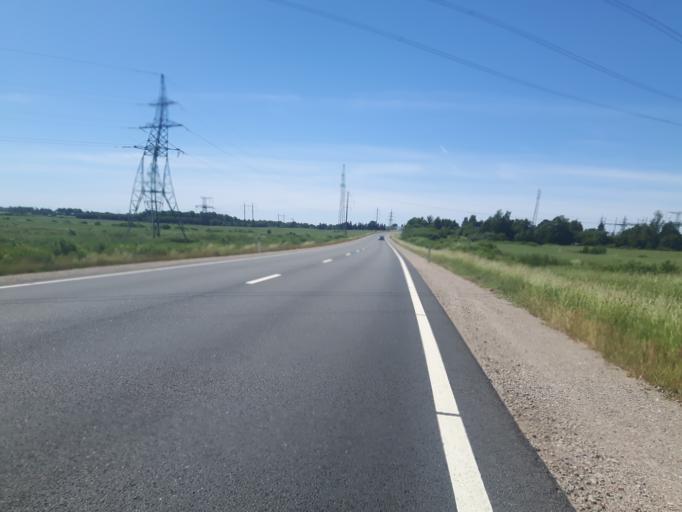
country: LV
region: Grobina
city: Grobina
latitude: 56.5436
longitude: 21.2103
